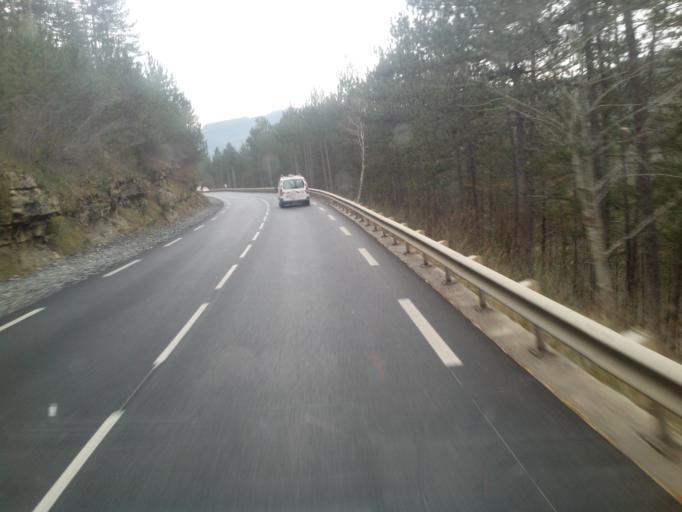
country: FR
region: Languedoc-Roussillon
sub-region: Departement de la Lozere
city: Mende
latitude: 44.5369
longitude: 3.4993
